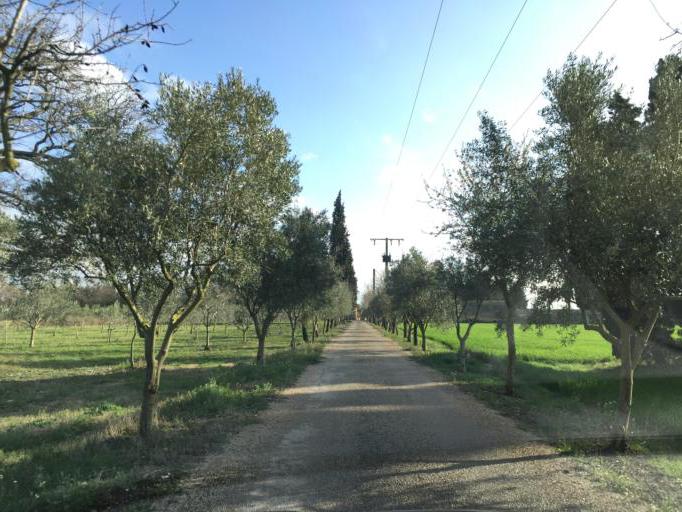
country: FR
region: Provence-Alpes-Cote d'Azur
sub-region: Departement du Vaucluse
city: Orange
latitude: 44.1396
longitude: 4.8323
